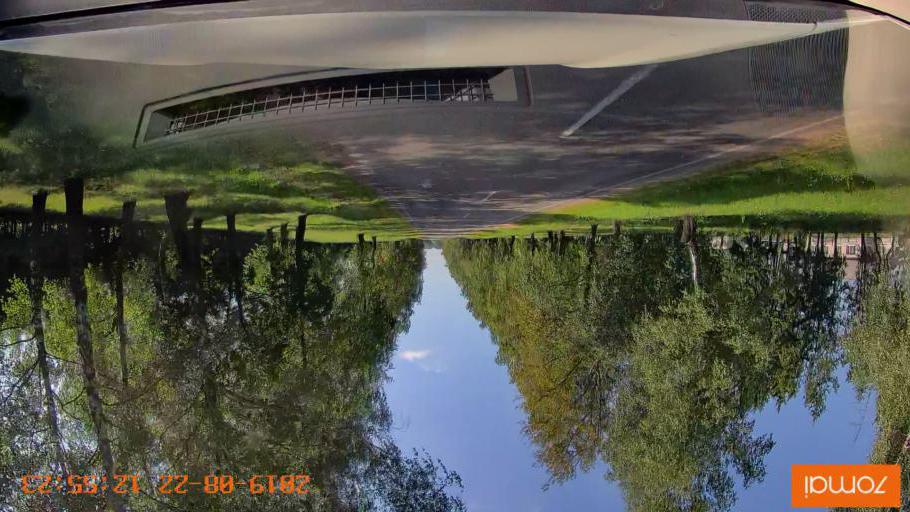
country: BY
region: Minsk
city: Prawdzinski
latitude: 53.4375
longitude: 27.7105
